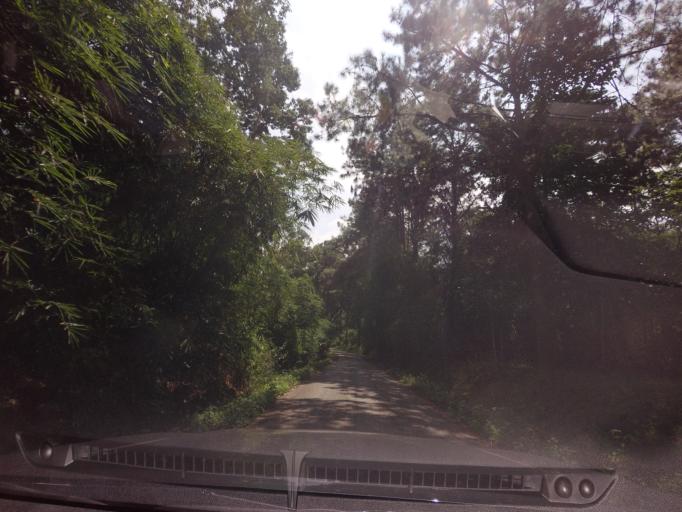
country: TH
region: Loei
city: Phu Ruea
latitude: 17.4791
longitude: 101.3523
